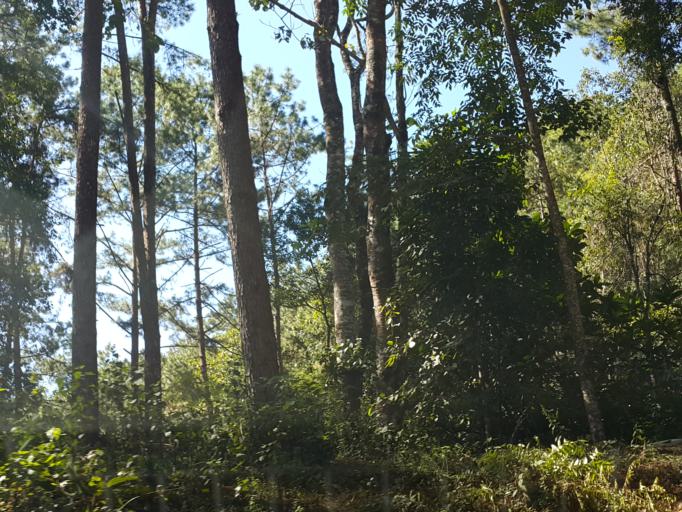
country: TH
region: Chiang Mai
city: Wiang Haeng
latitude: 19.5182
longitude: 98.8126
